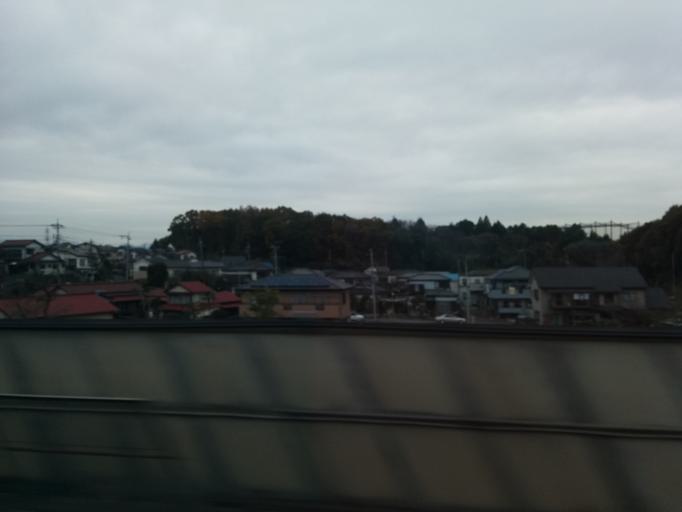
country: JP
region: Kanagawa
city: Minami-rinkan
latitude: 35.4226
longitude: 139.4435
